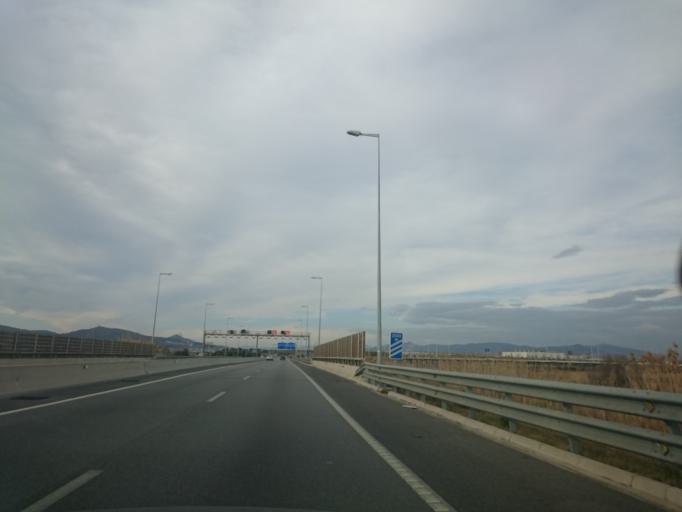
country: ES
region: Catalonia
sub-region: Provincia de Barcelona
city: Viladecans
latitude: 41.2886
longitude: 2.0520
